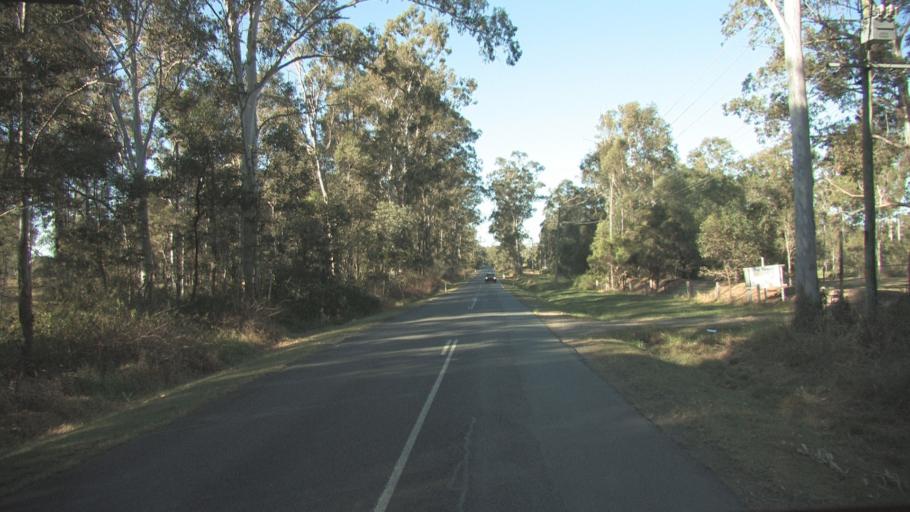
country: AU
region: Queensland
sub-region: Logan
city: Chambers Flat
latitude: -27.7804
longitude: 153.0665
